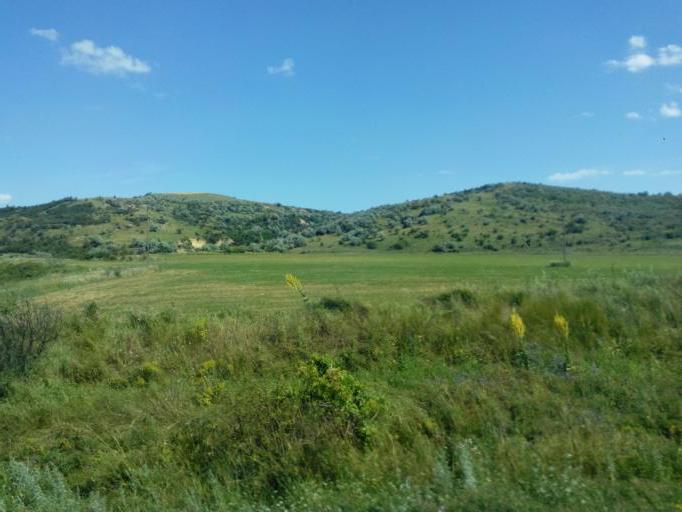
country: RO
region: Vaslui
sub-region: Comuna Banca
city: Banca
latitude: 46.3168
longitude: 27.7738
